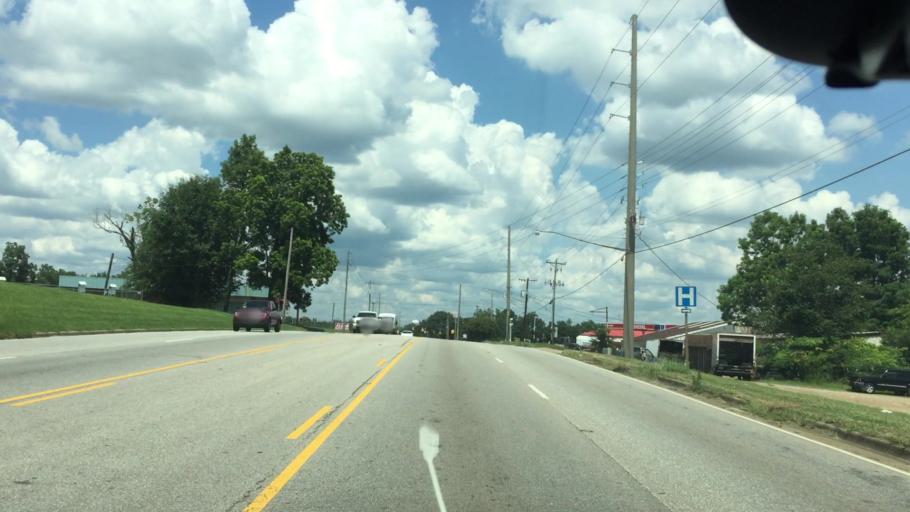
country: US
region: Alabama
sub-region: Pike County
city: Troy
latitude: 31.7899
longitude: -85.9790
